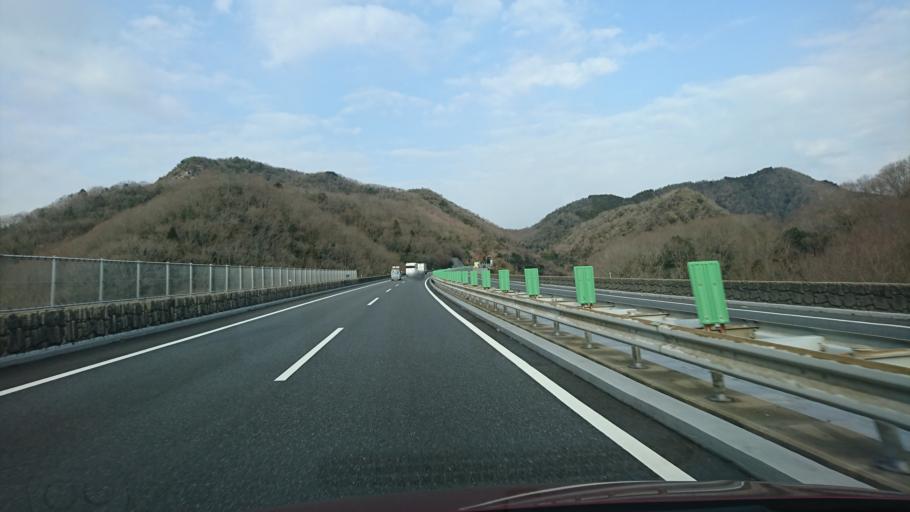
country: JP
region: Hyogo
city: Kariya
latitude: 34.7836
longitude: 134.2199
